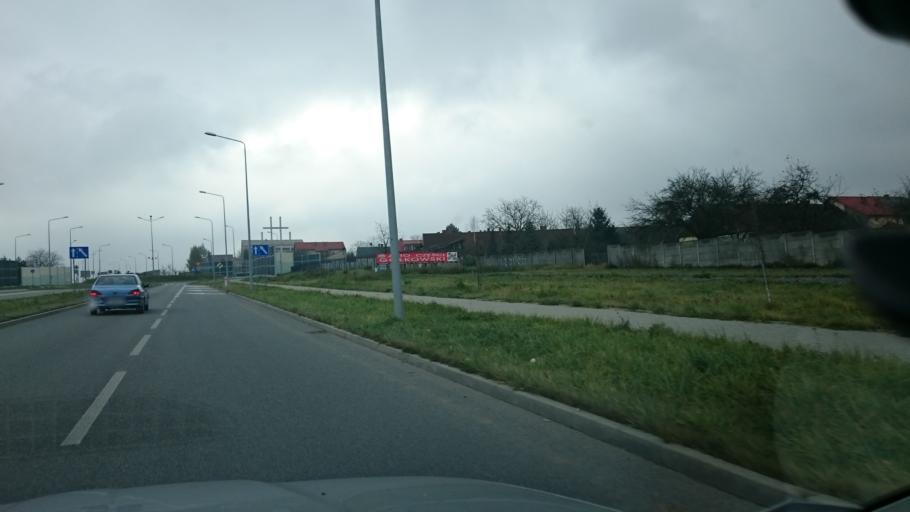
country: PL
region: Swietokrzyskie
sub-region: Powiat konecki
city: Konskie
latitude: 51.1946
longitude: 20.3990
